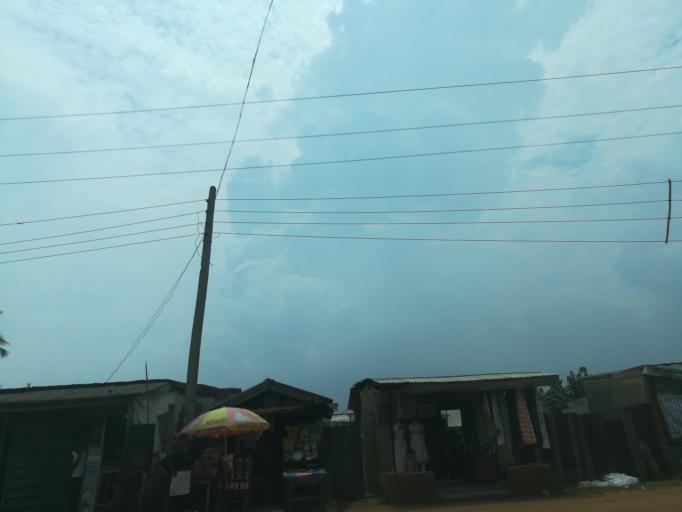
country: NG
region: Lagos
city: Ikorodu
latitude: 6.5961
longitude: 3.5887
